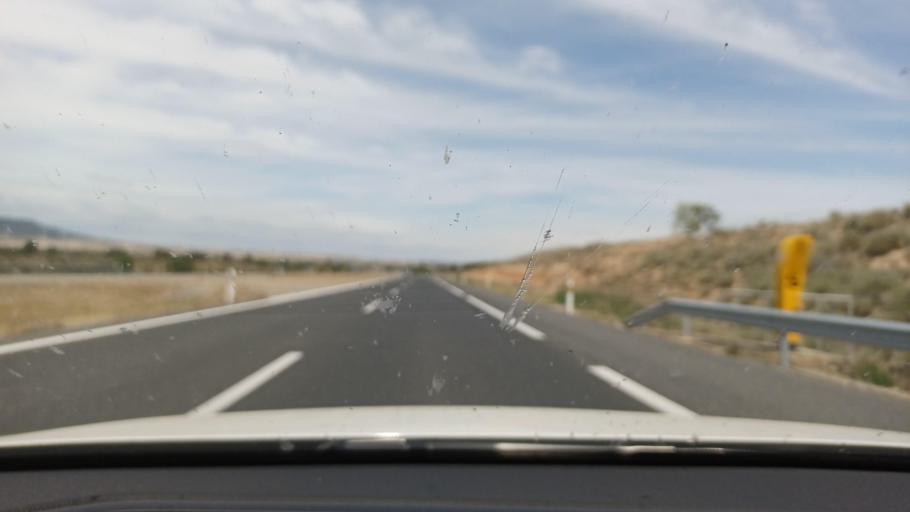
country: ES
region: Aragon
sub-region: Provincia de Zaragoza
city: Mallen
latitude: 41.8866
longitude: -1.4155
